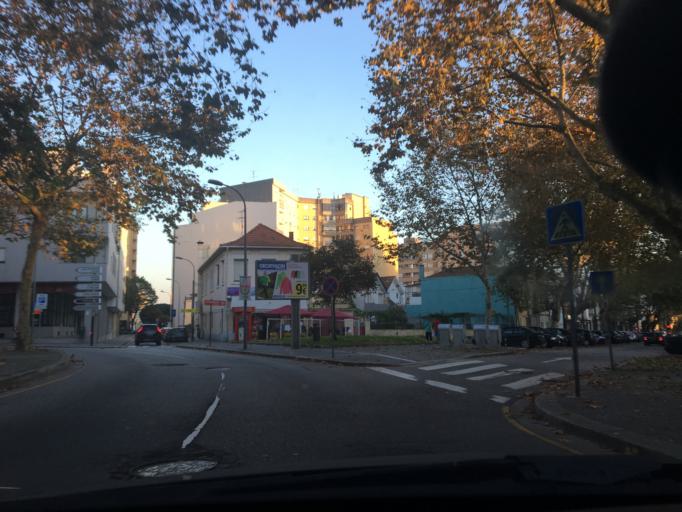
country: PT
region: Porto
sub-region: Matosinhos
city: Matosinhos
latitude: 41.1820
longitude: -8.6840
